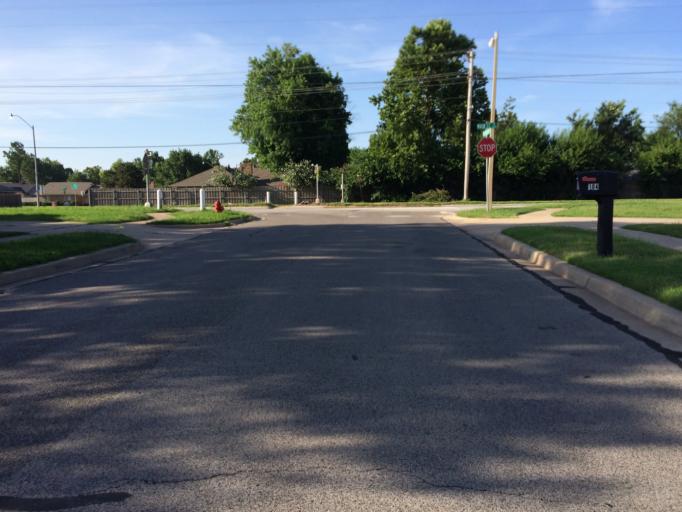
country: US
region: Oklahoma
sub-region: Cleveland County
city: Norman
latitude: 35.2188
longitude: -97.5004
